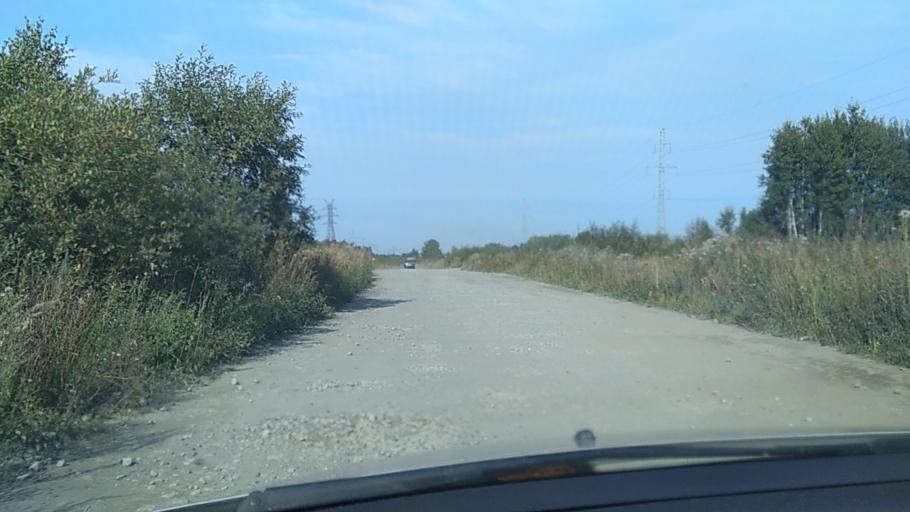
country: RU
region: Sverdlovsk
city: Sredneuralsk
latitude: 56.9724
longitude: 60.4745
